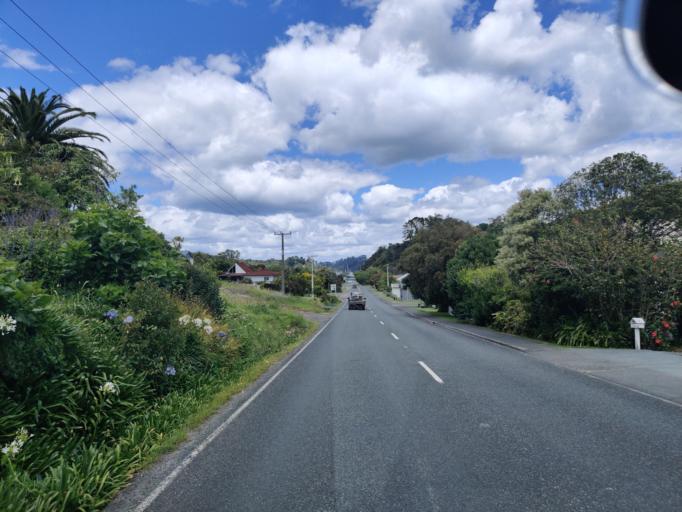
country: NZ
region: Northland
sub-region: Far North District
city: Paihia
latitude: -35.2643
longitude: 174.1241
